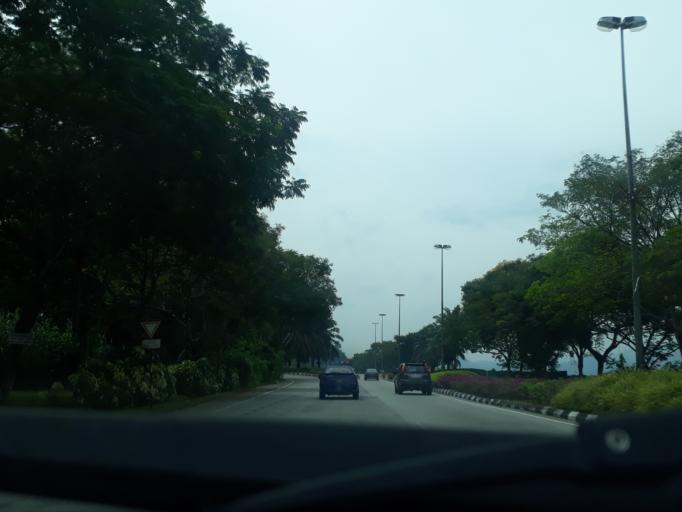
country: MY
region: Perak
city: Ipoh
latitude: 4.6334
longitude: 101.1542
